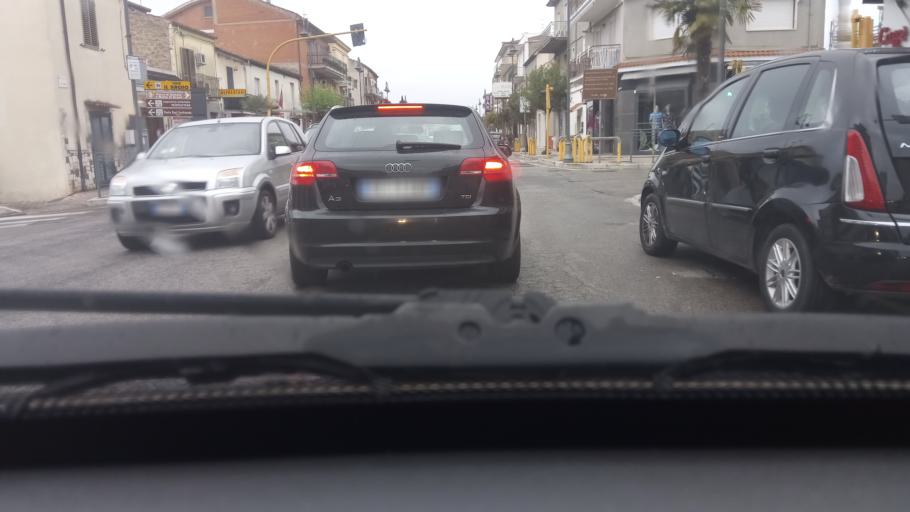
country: IT
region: Latium
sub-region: Provincia di Latina
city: Minturno
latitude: 41.2488
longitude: 13.7409
